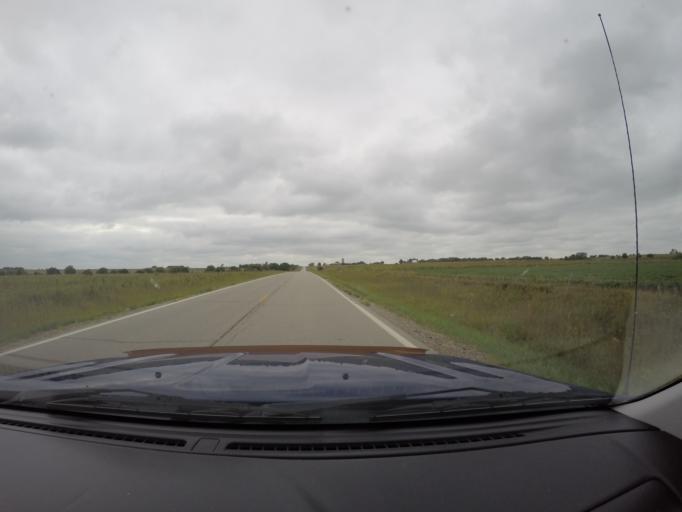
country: US
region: Kansas
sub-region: Morris County
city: Council Grove
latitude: 38.7976
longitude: -96.6950
